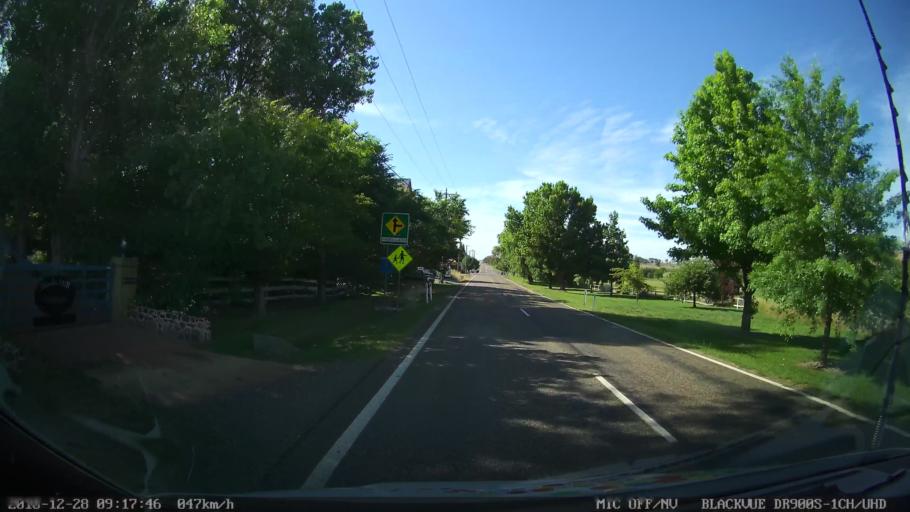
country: AU
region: New South Wales
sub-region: Upper Lachlan Shire
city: Crookwell
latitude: -34.3222
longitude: 149.3621
